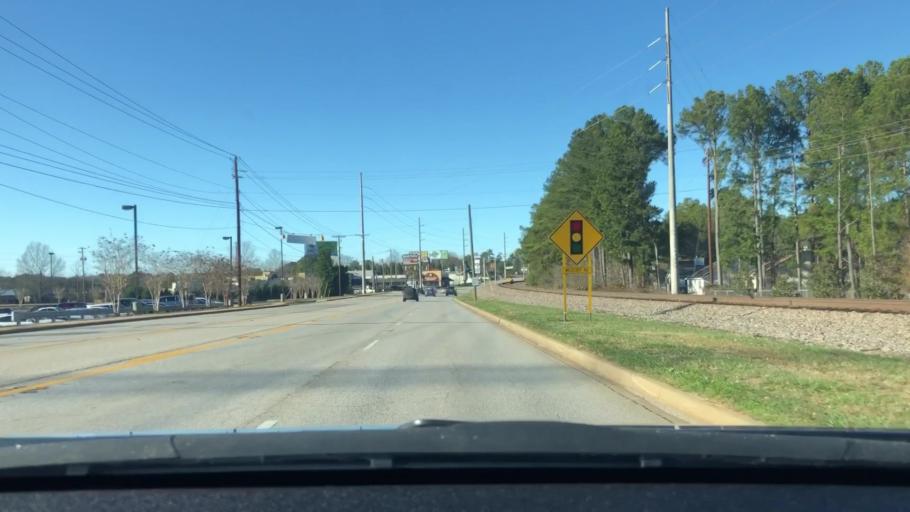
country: US
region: South Carolina
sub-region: Lexington County
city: Irmo
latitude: 34.0699
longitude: -81.1734
